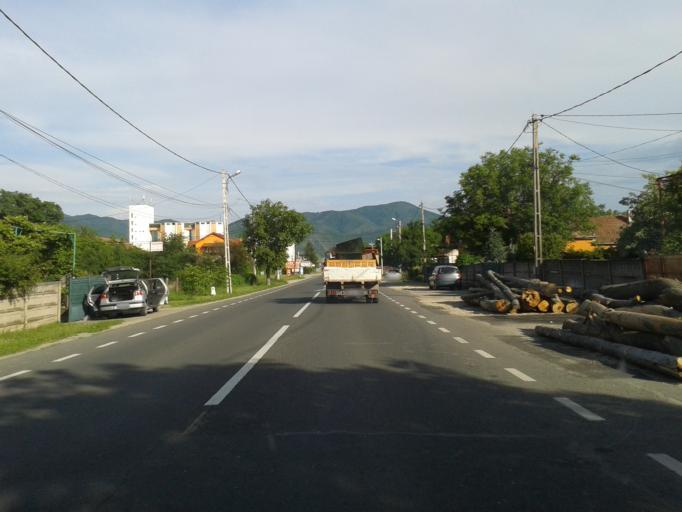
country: RO
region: Hunedoara
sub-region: Oras Hateg
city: Hateg
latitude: 45.6012
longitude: 22.9579
